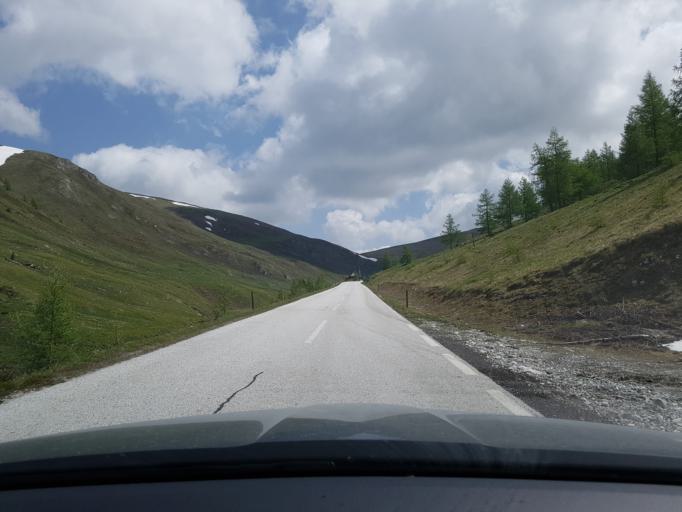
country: AT
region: Salzburg
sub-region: Politischer Bezirk Tamsweg
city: Thomatal
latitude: 46.9444
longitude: 13.7457
